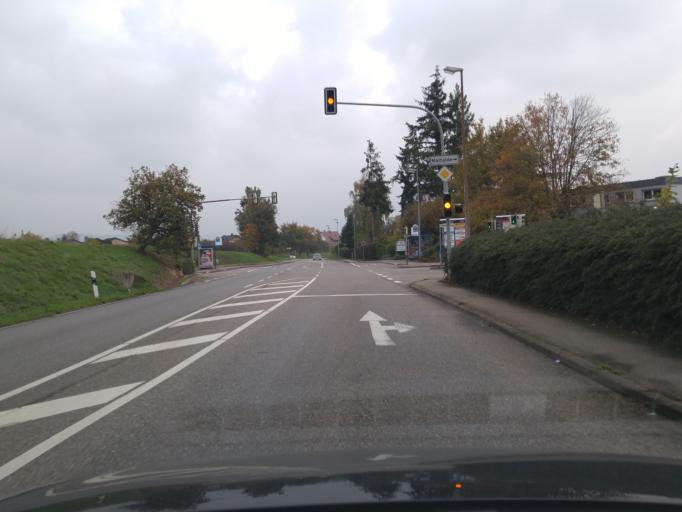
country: DE
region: Baden-Wuerttemberg
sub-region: Regierungsbezirk Stuttgart
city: Leingarten
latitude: 49.1646
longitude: 9.1665
